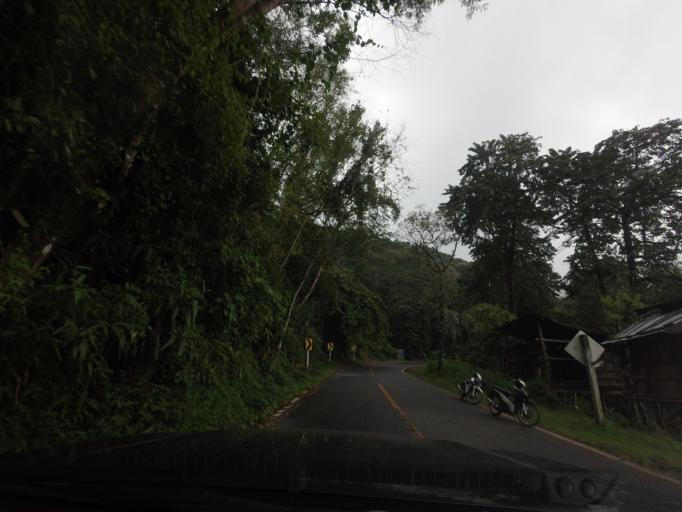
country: TH
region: Nan
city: Bo Kluea
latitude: 19.1804
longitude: 101.0818
